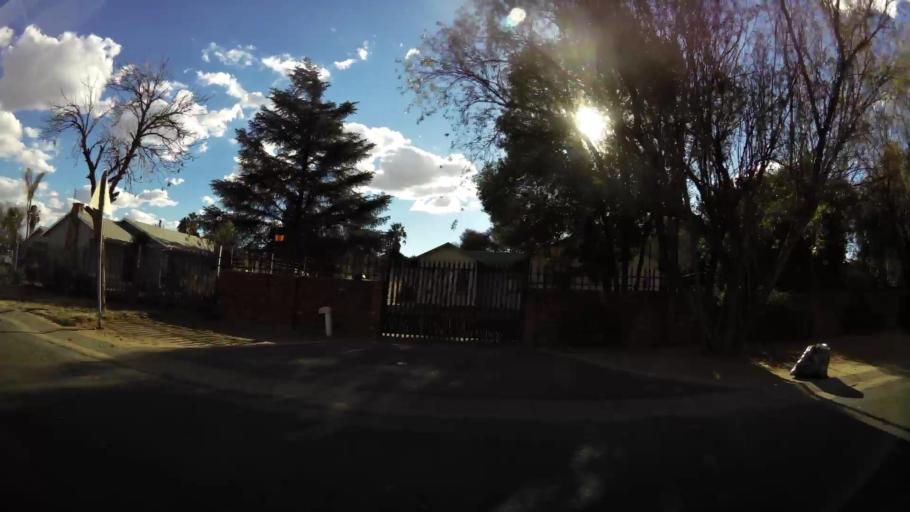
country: ZA
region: North-West
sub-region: Dr Kenneth Kaunda District Municipality
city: Klerksdorp
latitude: -26.8343
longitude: 26.6612
